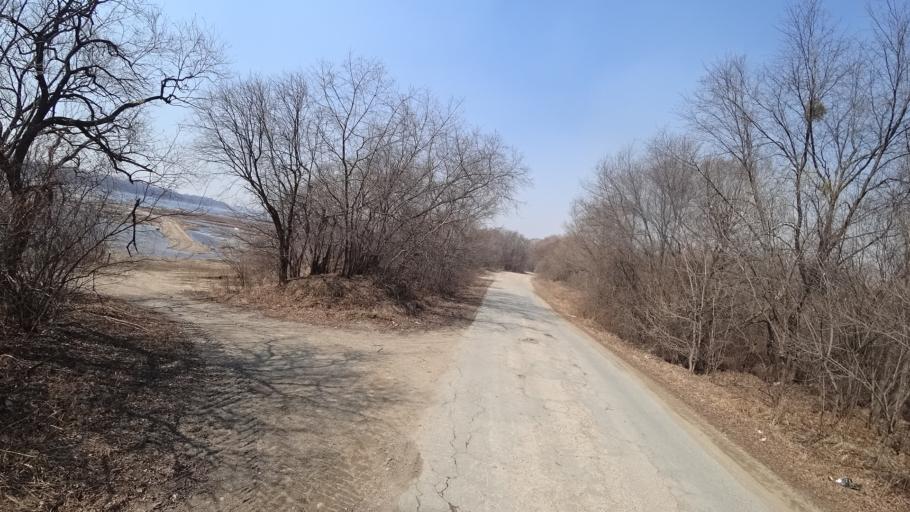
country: RU
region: Amur
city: Novobureyskiy
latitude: 49.7885
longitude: 129.9092
